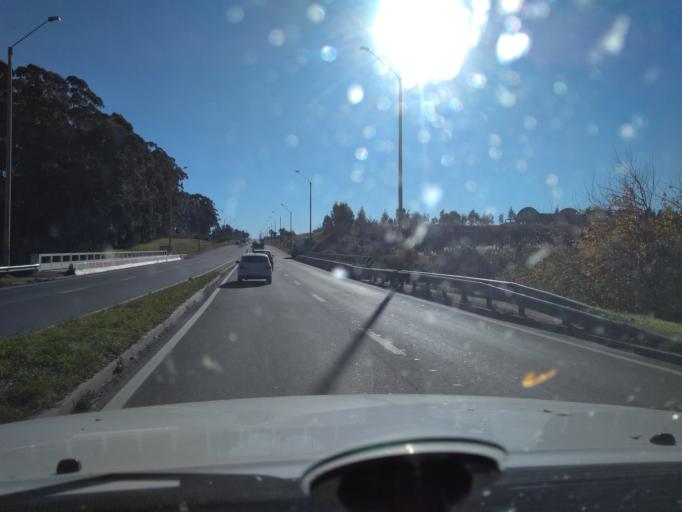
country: UY
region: Canelones
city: Colonia Nicolich
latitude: -34.8073
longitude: -56.0459
